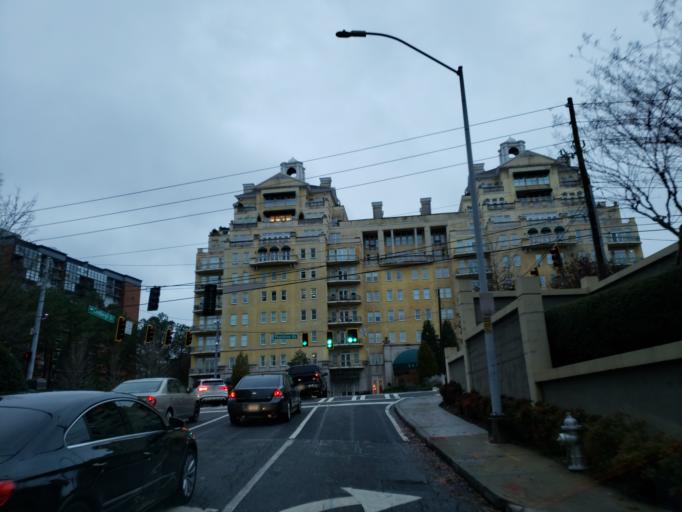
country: US
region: Georgia
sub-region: DeKalb County
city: North Atlanta
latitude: 33.8229
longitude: -84.3871
